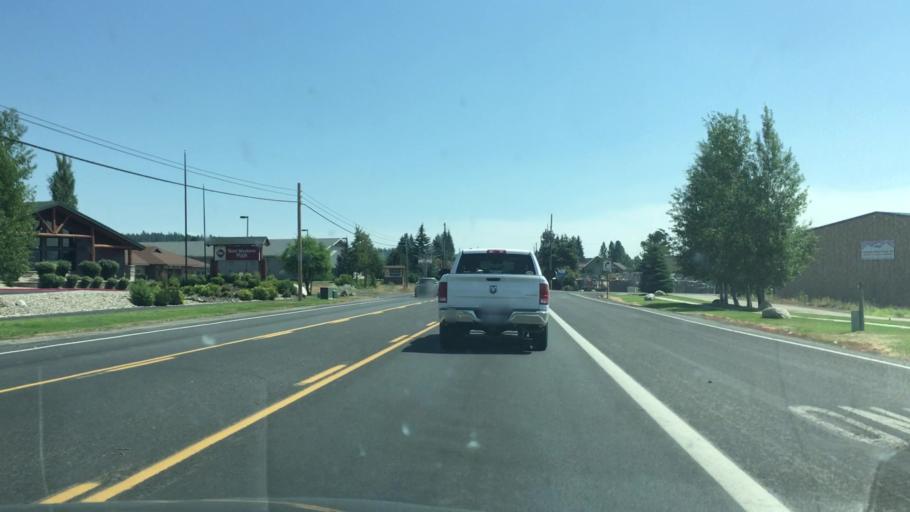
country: US
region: Idaho
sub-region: Valley County
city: McCall
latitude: 44.8964
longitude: -116.0960
